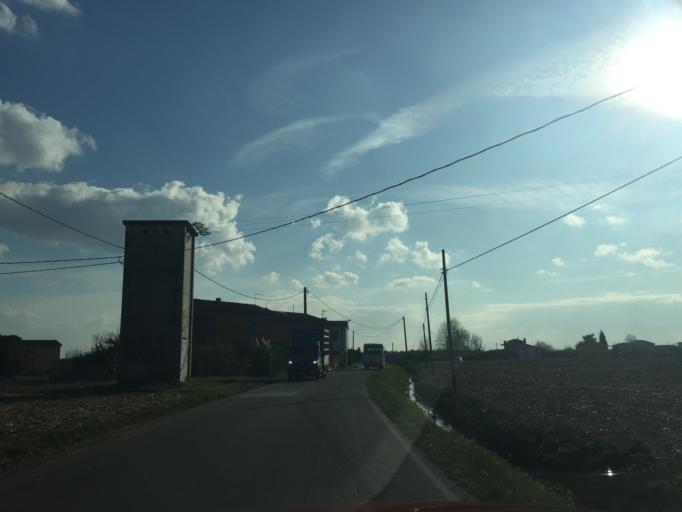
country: IT
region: Tuscany
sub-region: Provincia di Pistoia
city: Ponte Buggianese
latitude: 43.8313
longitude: 10.7428
